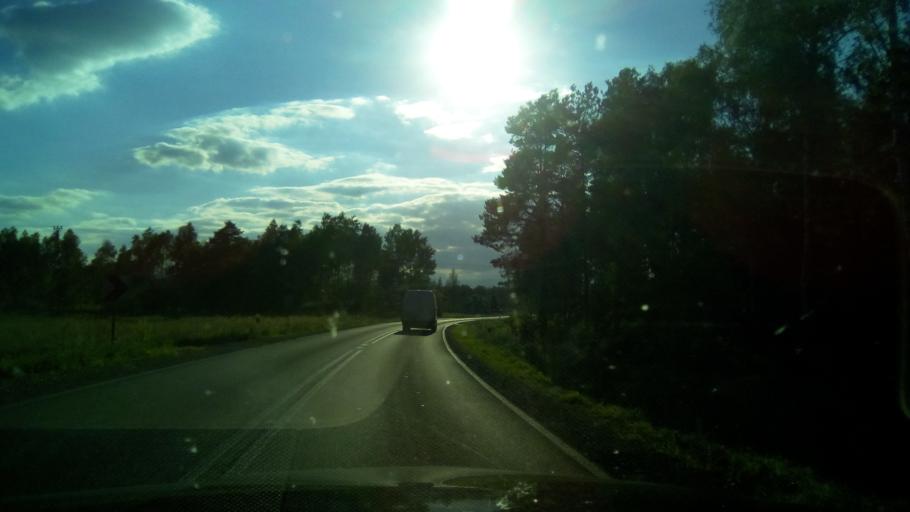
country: PL
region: Masovian Voivodeship
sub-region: Powiat bialobrzeski
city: Stromiec
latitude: 51.6439
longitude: 21.1470
